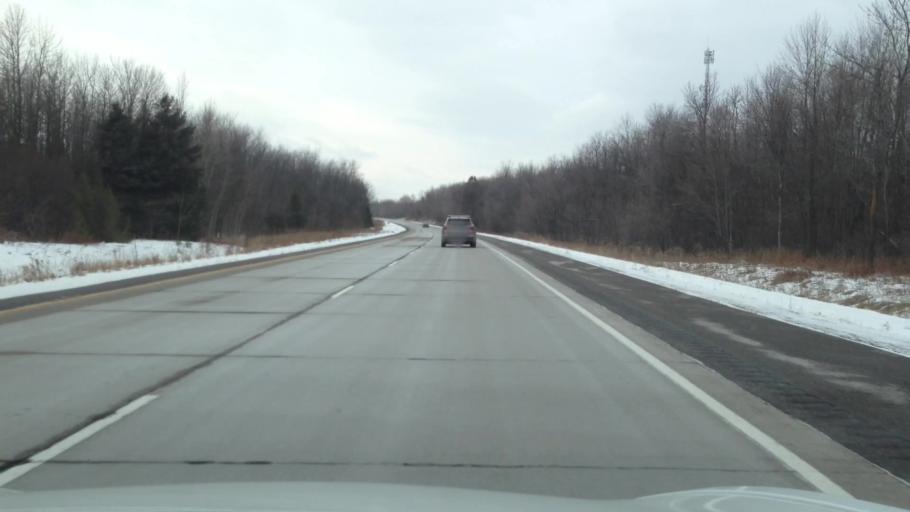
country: CA
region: Ontario
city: Hawkesbury
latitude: 45.5041
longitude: -74.5919
